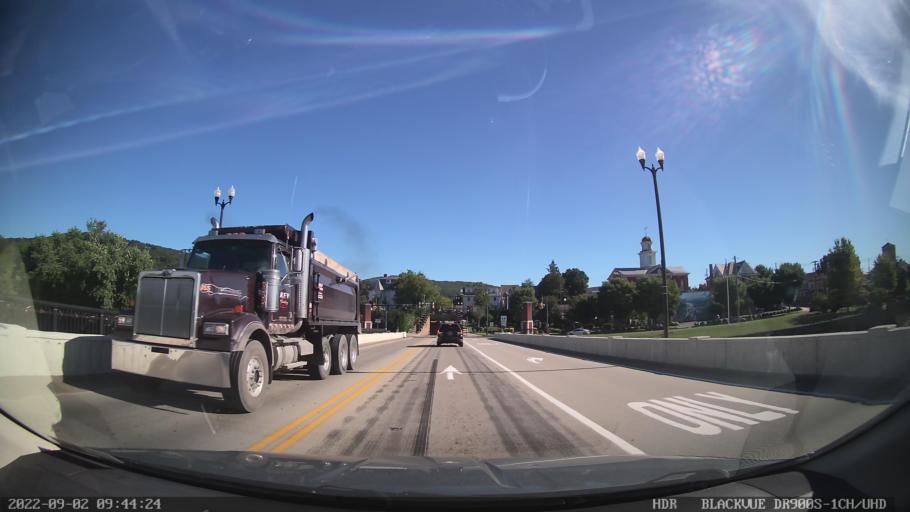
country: US
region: Pennsylvania
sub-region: Northumberland County
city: Riverside
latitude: 40.9589
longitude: -76.6218
